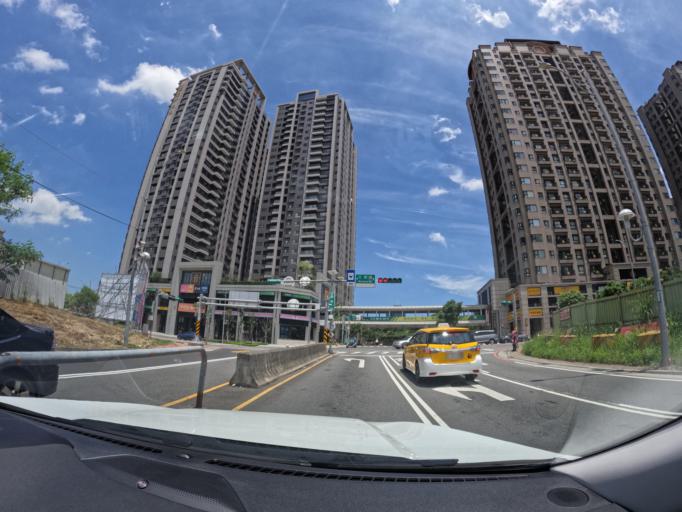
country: TW
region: Taipei
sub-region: Taipei
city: Banqiao
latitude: 25.0398
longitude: 121.3870
